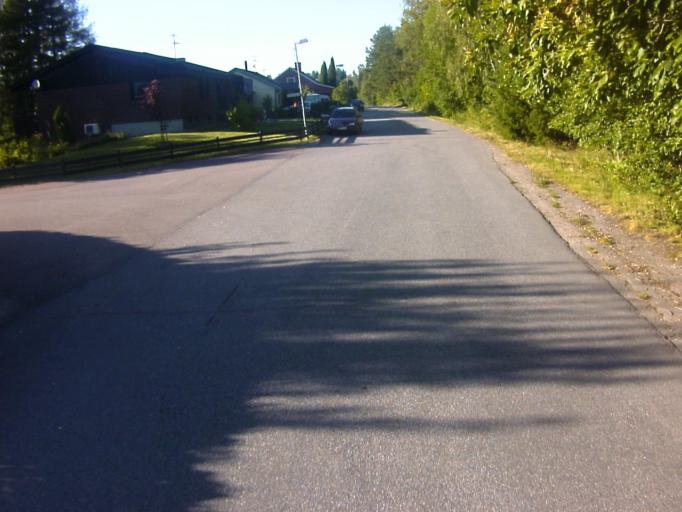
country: SE
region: Soedermanland
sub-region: Eskilstuna Kommun
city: Skogstorp
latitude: 59.3319
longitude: 16.4359
